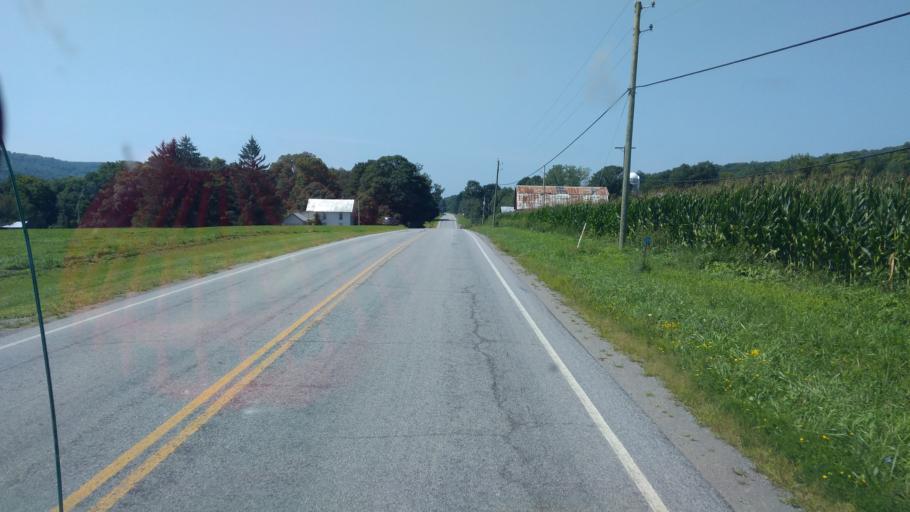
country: US
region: New York
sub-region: Allegany County
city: Belmont
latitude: 42.3029
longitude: -77.9731
